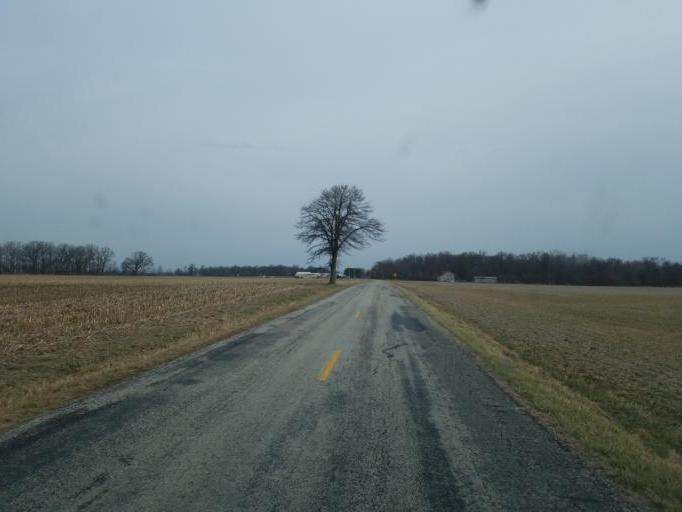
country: US
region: Ohio
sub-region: Marion County
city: Marion
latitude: 40.5904
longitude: -82.9974
